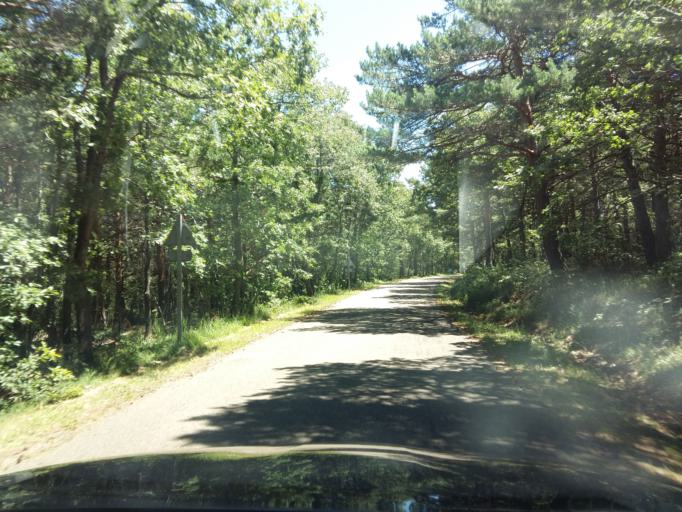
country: ES
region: Castille and Leon
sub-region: Provincia de Soria
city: Vozmediano
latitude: 41.8179
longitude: -1.8240
